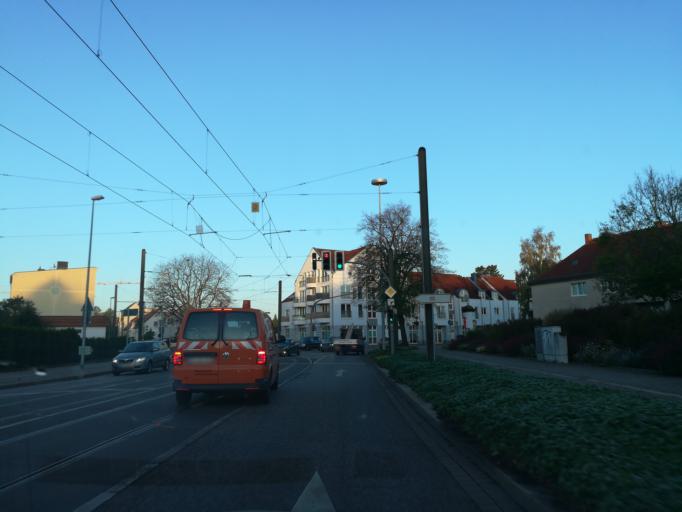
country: DE
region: Saxony-Anhalt
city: Diesdorf
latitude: 52.1294
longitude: 11.5744
